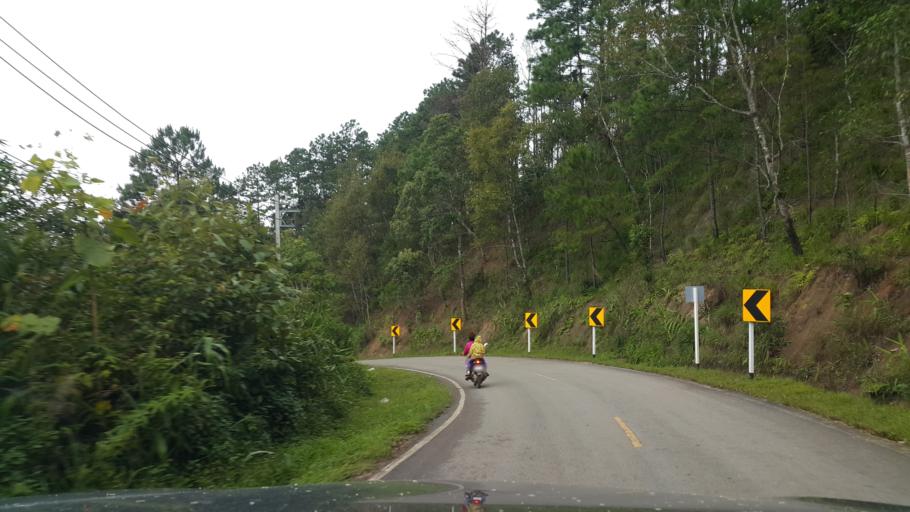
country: TH
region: Chiang Mai
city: Samoeng
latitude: 18.8800
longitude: 98.5158
